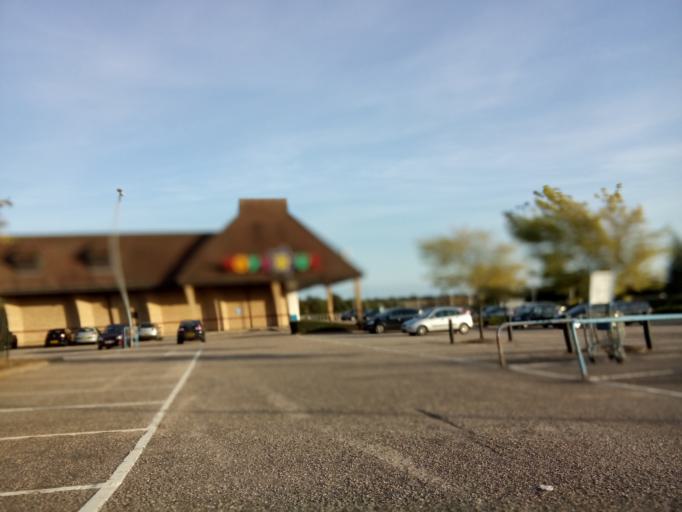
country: GB
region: England
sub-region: Suffolk
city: Bramford
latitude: 52.0381
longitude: 1.0982
